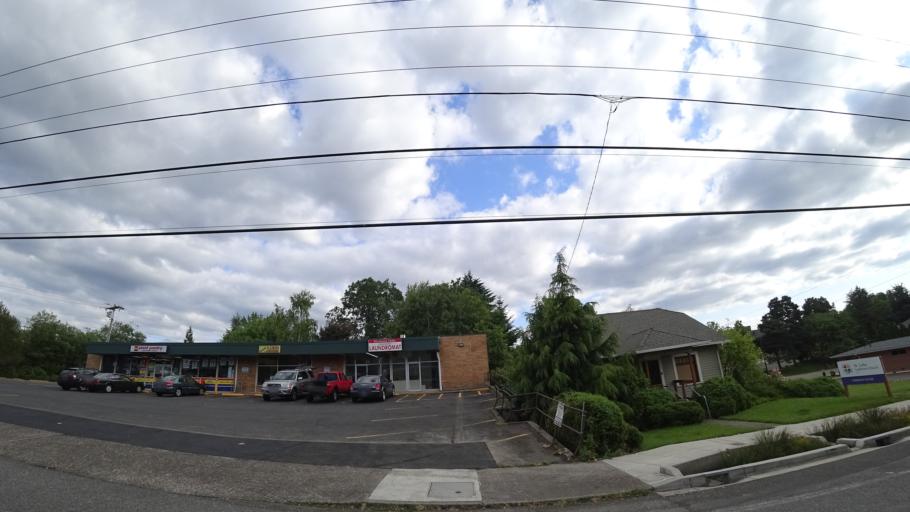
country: US
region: Oregon
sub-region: Washington County
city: Garden Home-Whitford
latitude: 45.4762
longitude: -122.7238
